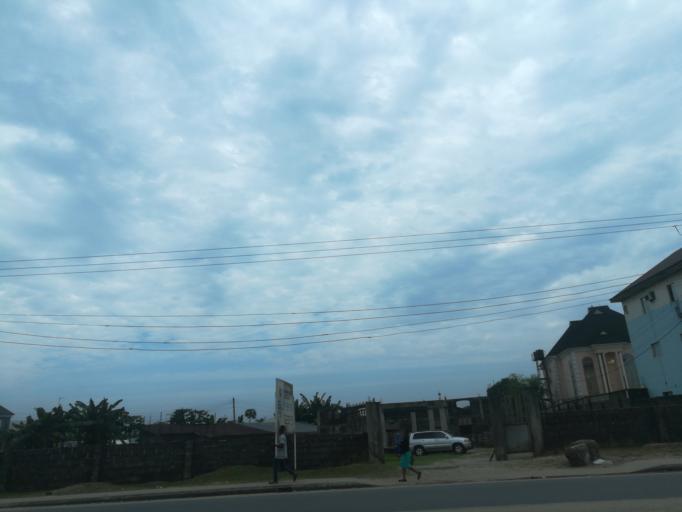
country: NG
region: Rivers
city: Port Harcourt
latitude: 4.8143
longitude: 6.9507
